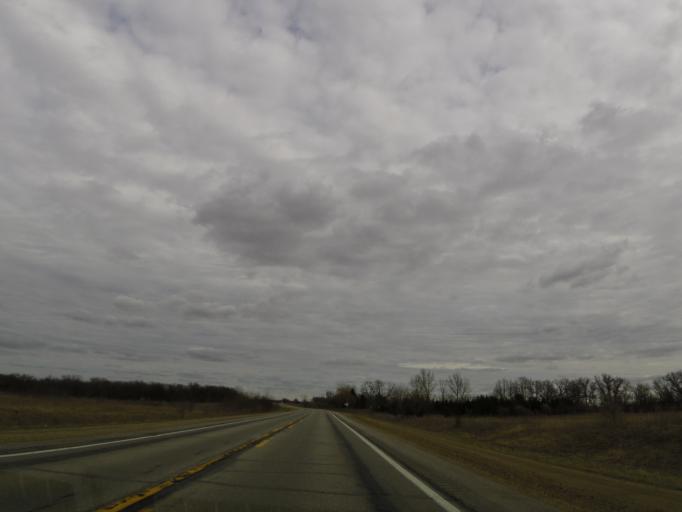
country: US
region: Minnesota
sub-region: Fillmore County
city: Spring Valley
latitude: 43.4744
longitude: -92.3310
